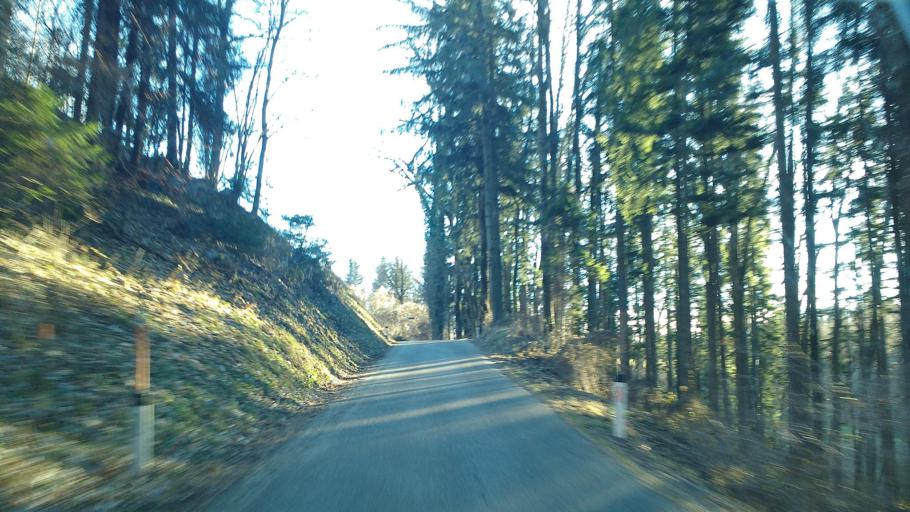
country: AT
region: Upper Austria
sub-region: Politischer Bezirk Kirchdorf an der Krems
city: Micheldorf in Oberoesterreich
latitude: 47.9057
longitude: 14.1486
